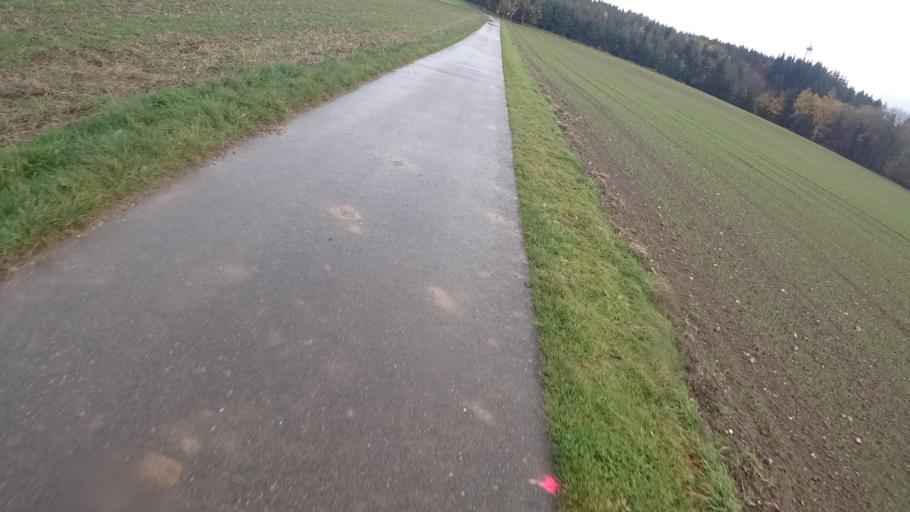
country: DE
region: Rheinland-Pfalz
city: Godenroth
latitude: 50.1084
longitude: 7.4994
